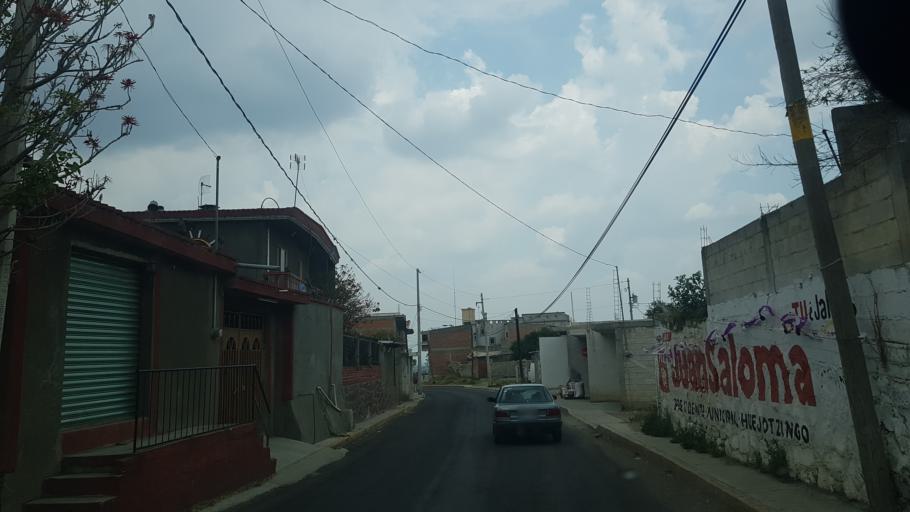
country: MX
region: Puebla
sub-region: Huejotzingo
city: San Miguel Tianguizolco
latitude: 19.1591
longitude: -98.4390
